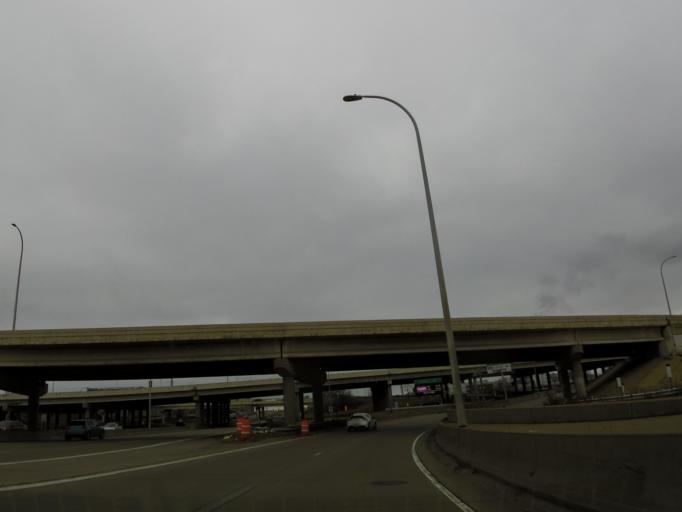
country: US
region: Minnesota
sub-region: Hennepin County
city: Minneapolis
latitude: 44.9739
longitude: -93.2873
